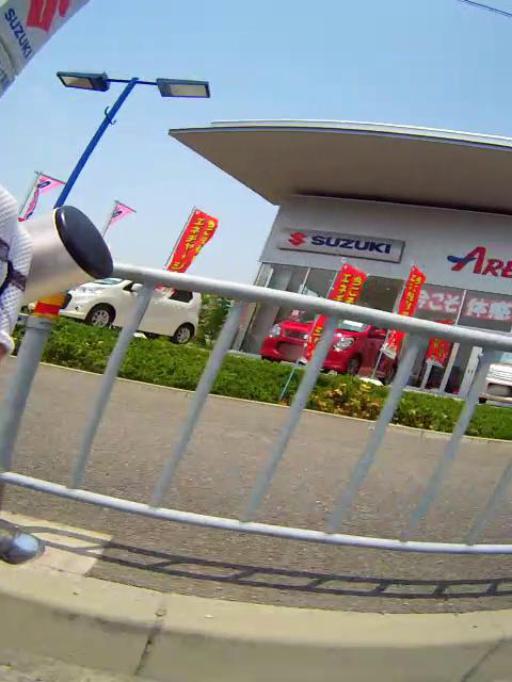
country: JP
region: Osaka
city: Mino
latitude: 34.8276
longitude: 135.4806
